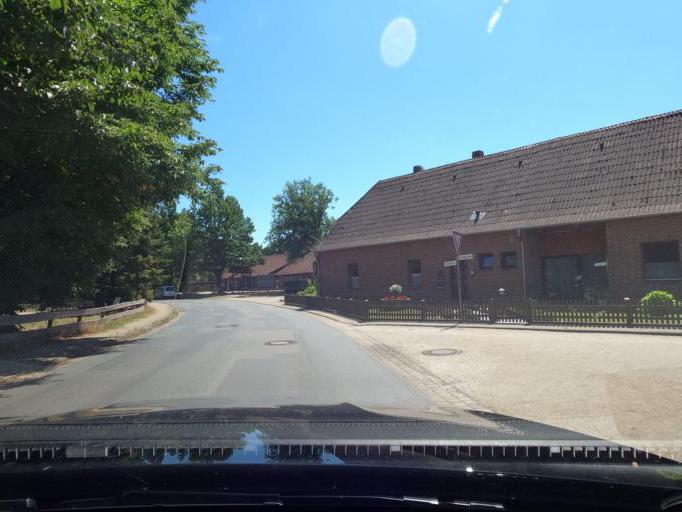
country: DE
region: Lower Saxony
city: Muden
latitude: 52.5275
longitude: 10.3560
